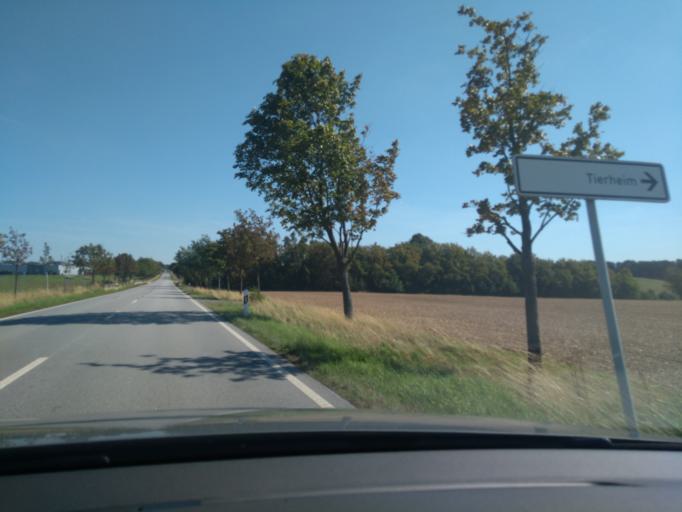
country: DE
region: Saxony
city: Goda
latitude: 51.1945
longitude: 14.3343
